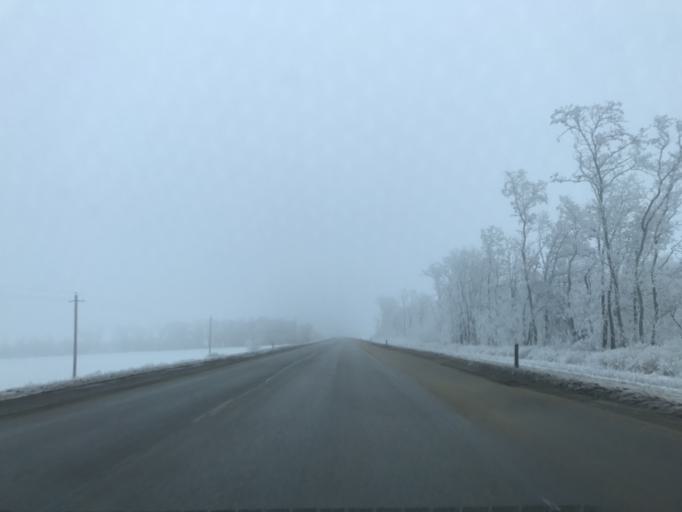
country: RU
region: Rostov
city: Temernik
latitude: 47.3782
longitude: 39.8199
